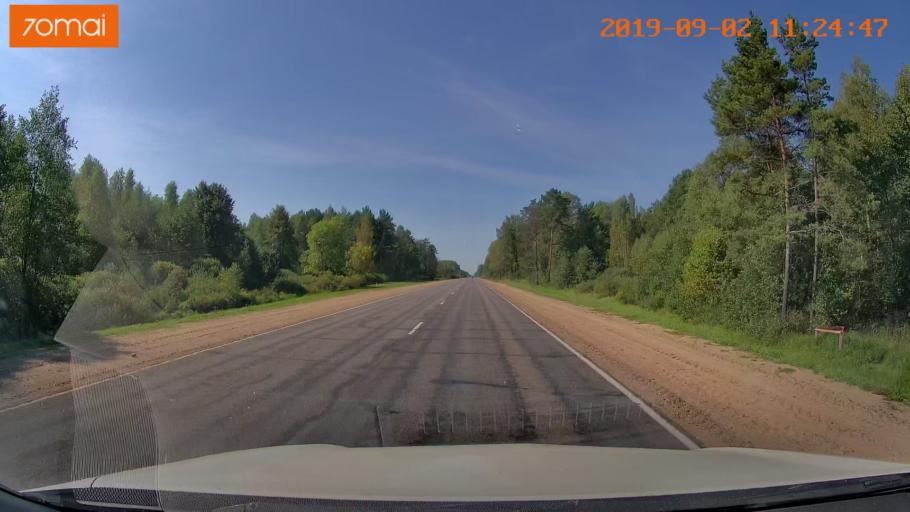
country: RU
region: Smolensk
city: Roslavl'
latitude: 54.0074
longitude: 32.9680
